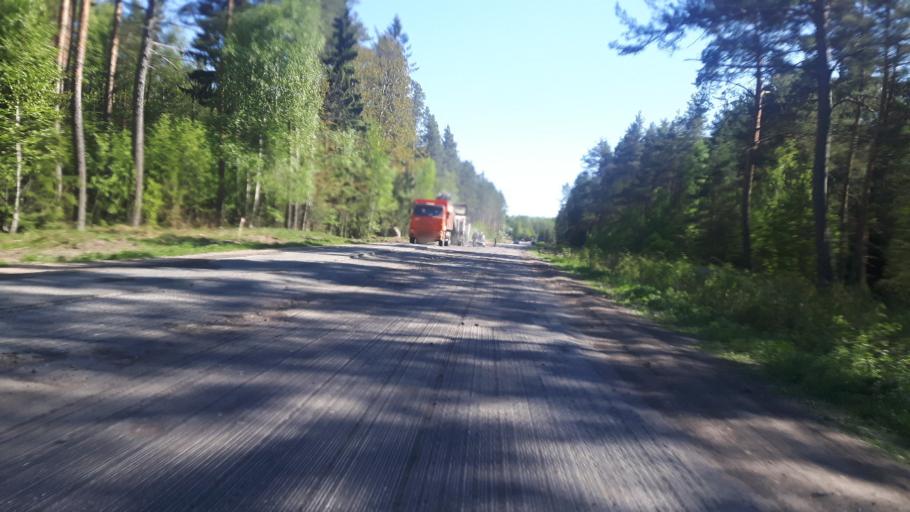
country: RU
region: Leningrad
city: Sosnovyy Bor
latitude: 60.2263
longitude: 29.0054
